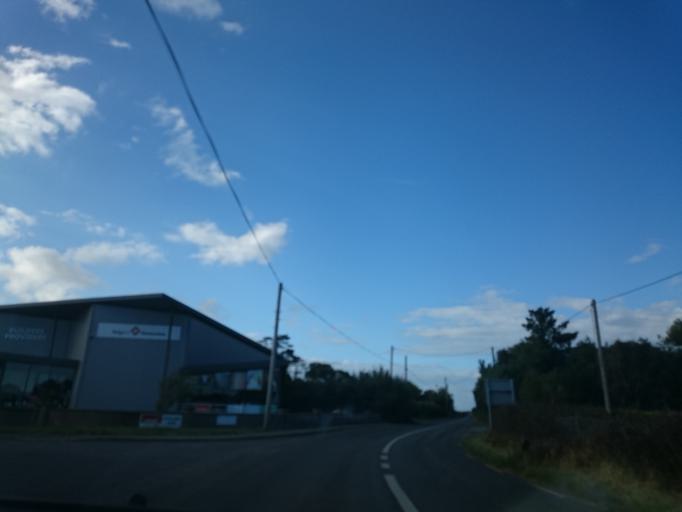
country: IE
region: Leinster
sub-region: Loch Garman
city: Loch Garman
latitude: 52.2438
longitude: -6.4896
